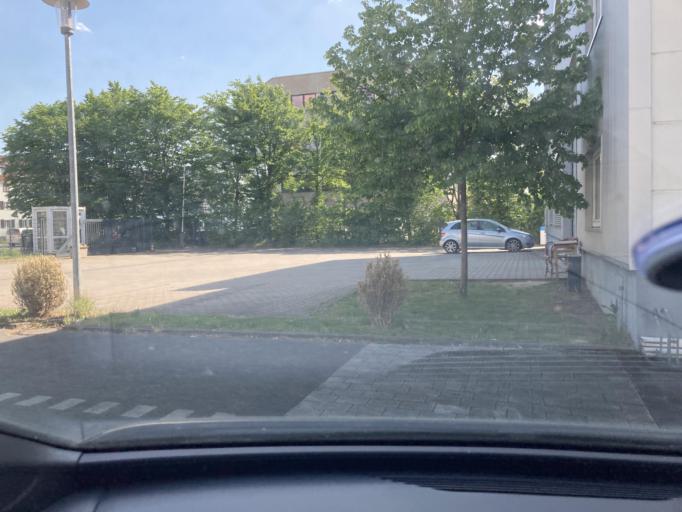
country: DE
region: Hesse
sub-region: Regierungsbezirk Darmstadt
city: Offenbach
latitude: 50.0904
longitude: 8.7495
